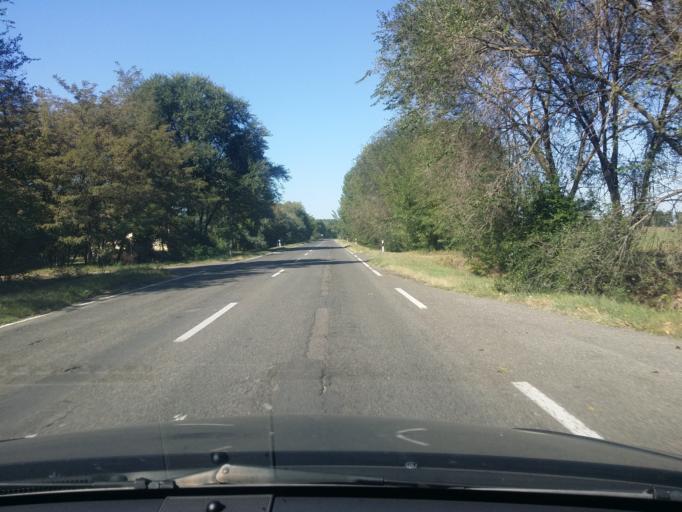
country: HU
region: Bacs-Kiskun
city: Palmonostora
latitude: 46.6146
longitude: 19.9081
